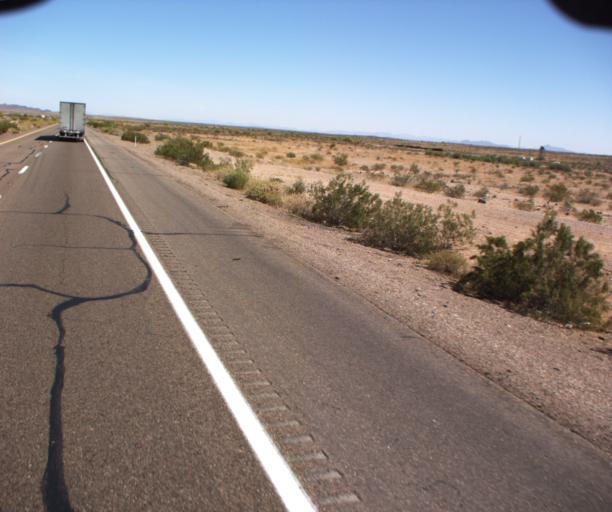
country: US
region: Arizona
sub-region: Maricopa County
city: Gila Bend
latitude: 32.8727
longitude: -113.1314
